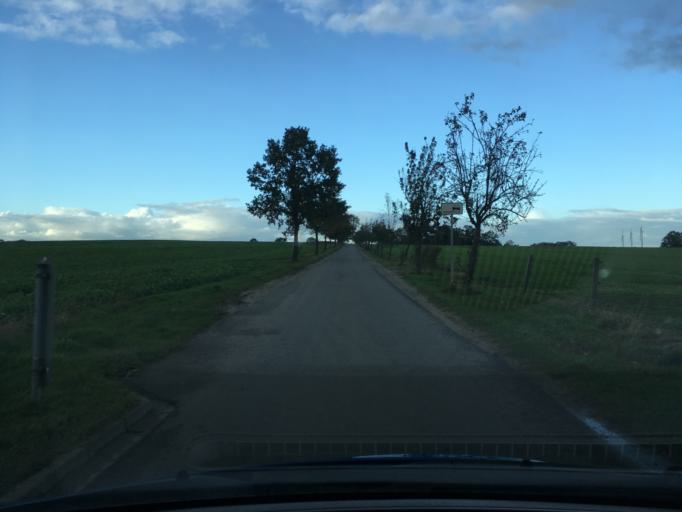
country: DE
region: Lower Saxony
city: Reinstorf
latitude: 53.2366
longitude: 10.5684
